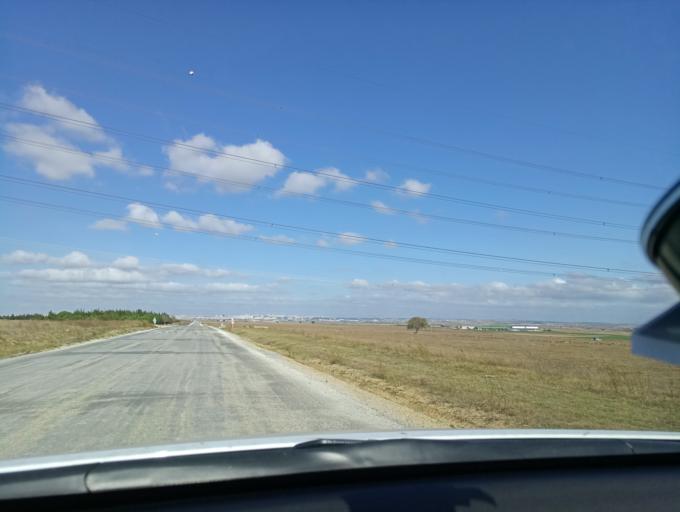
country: TR
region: Tekirdag
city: Corlu
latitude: 41.0599
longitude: 27.8345
